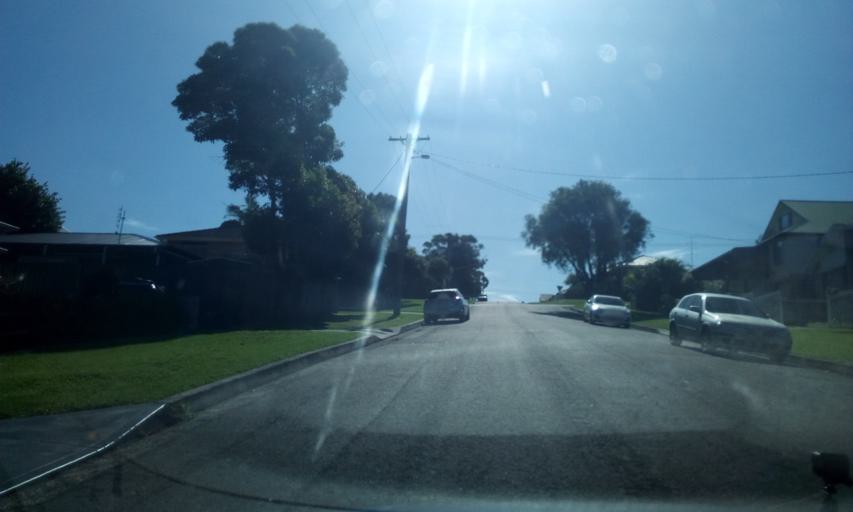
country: AU
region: New South Wales
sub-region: Wollongong
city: Bulli
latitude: -34.3406
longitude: 150.9171
